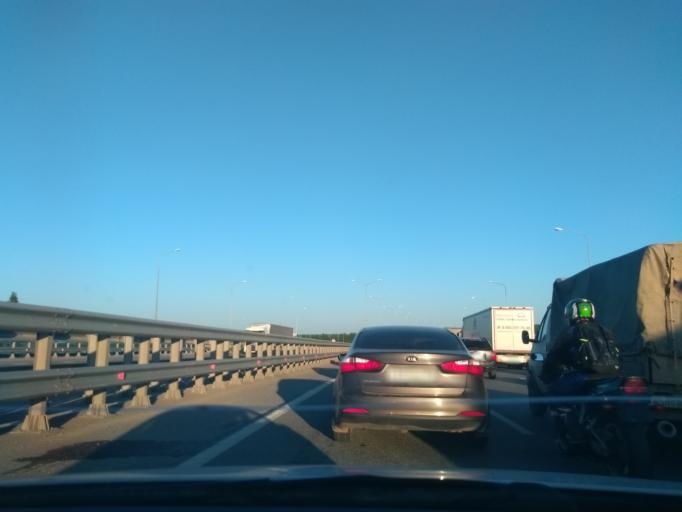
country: RU
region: Perm
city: Lobanovo
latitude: 57.8445
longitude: 56.2935
